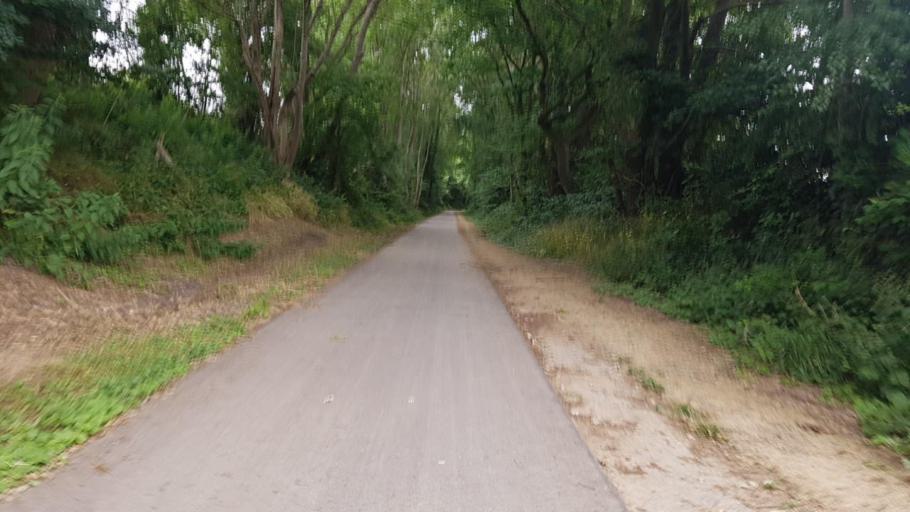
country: BE
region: Wallonia
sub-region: Province de Liege
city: Plombieres
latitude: 50.7347
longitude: 5.9520
